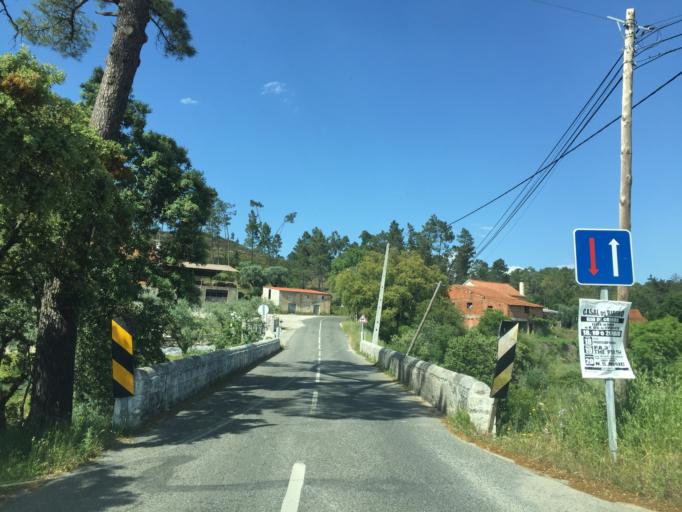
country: PT
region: Leiria
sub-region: Alvaiazere
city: Alvaiazere
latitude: 39.7799
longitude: -8.4558
